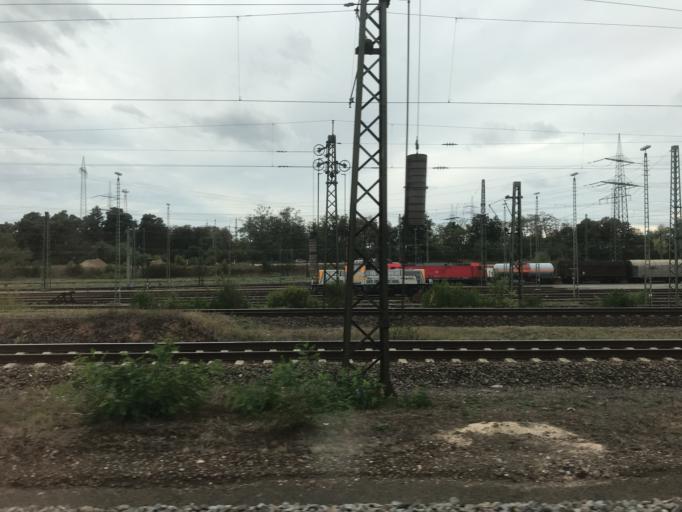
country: DE
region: Baden-Wuerttemberg
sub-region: Karlsruhe Region
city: Ilvesheim
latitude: 49.4474
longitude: 8.5478
